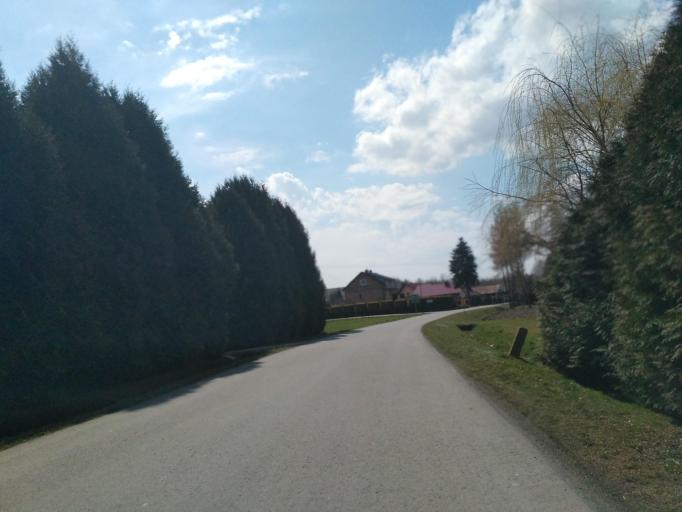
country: PL
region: Subcarpathian Voivodeship
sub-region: Powiat ropczycko-sedziszowski
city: Iwierzyce
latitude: 50.0032
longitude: 21.7603
